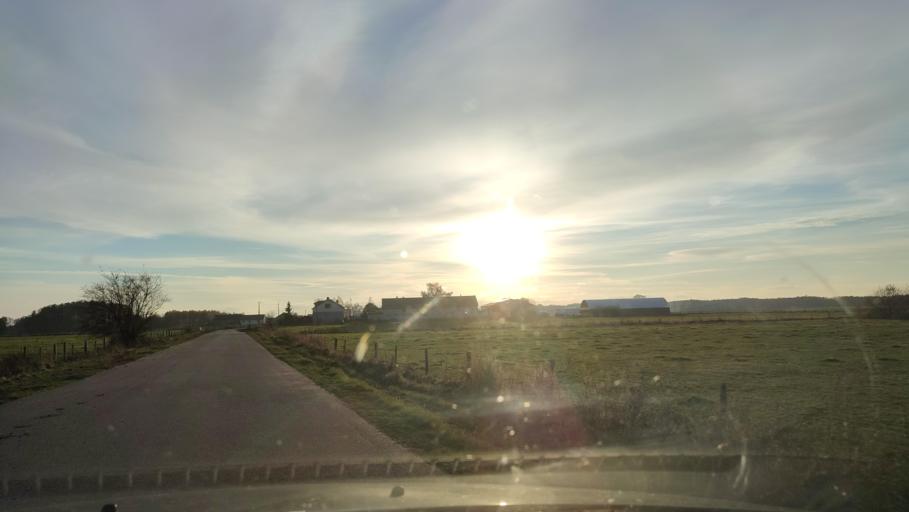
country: PL
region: Masovian Voivodeship
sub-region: Powiat mlawski
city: Dzierzgowo
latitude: 53.2840
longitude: 20.6543
